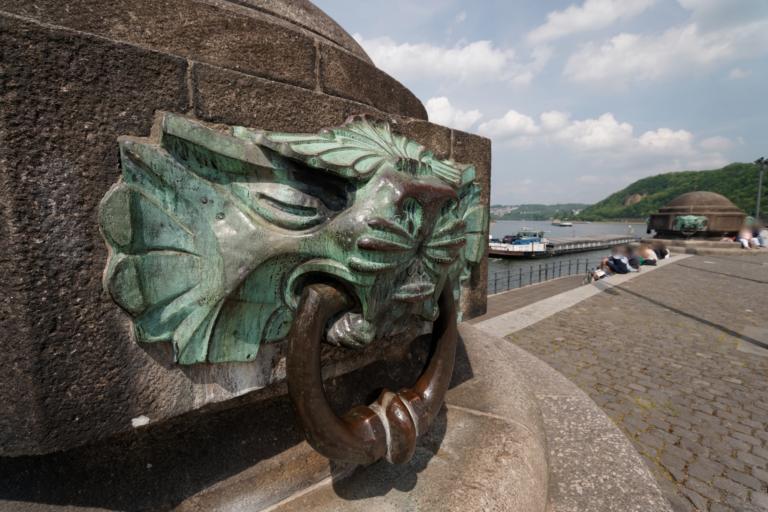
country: DE
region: Rheinland-Pfalz
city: Koblenz
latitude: 50.3645
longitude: 7.6054
